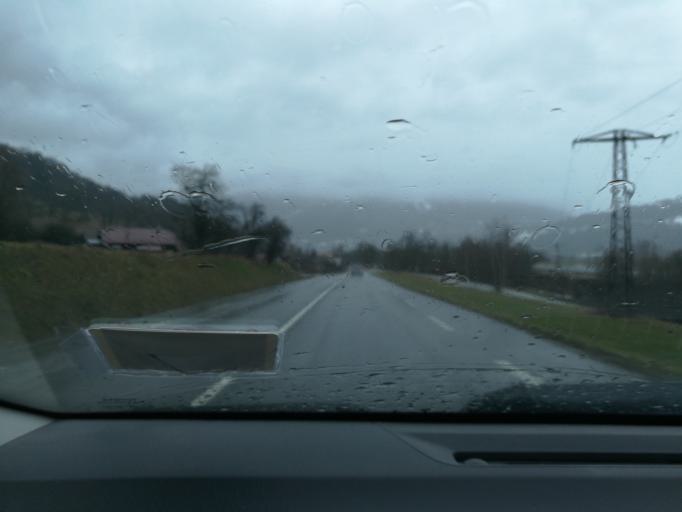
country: FR
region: Rhone-Alpes
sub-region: Departement de la Haute-Savoie
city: Domancy
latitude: 45.9235
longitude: 6.6625
